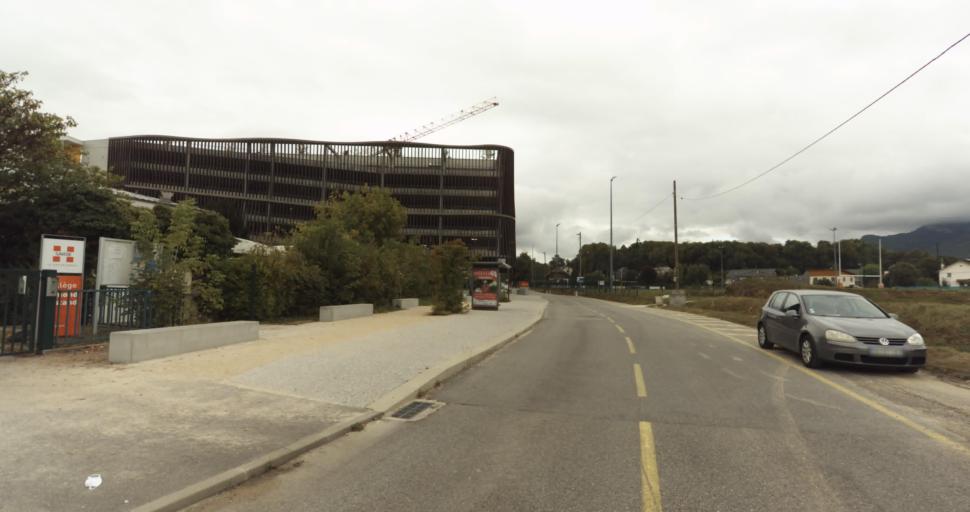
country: FR
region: Rhone-Alpes
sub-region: Departement de la Savoie
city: La Ravoire
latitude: 45.5601
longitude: 5.9654
